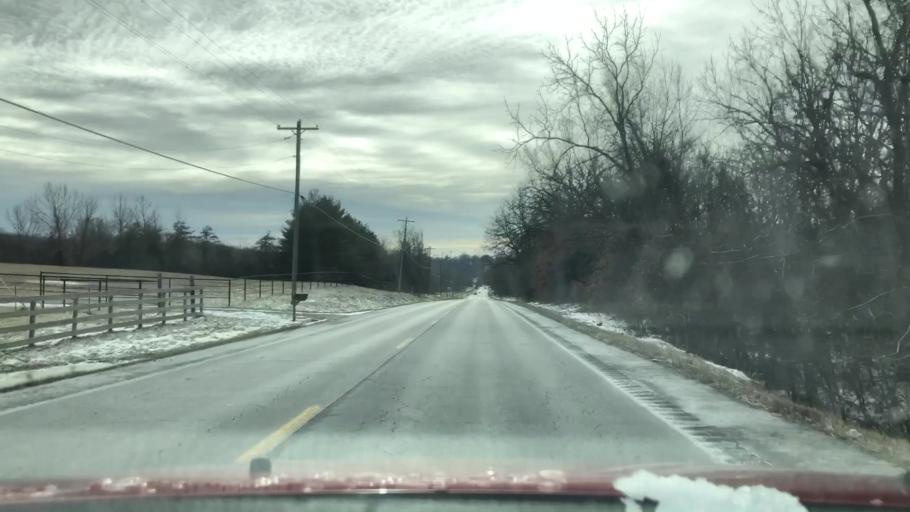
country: US
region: Missouri
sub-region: Jackson County
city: Oak Grove
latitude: 38.9500
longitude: -94.1317
